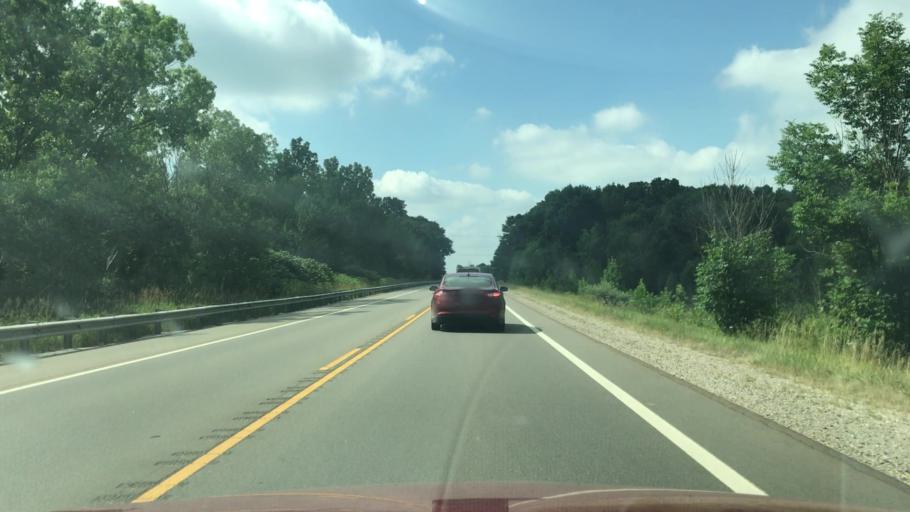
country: US
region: Michigan
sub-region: Kent County
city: Sparta
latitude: 43.1843
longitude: -85.7201
